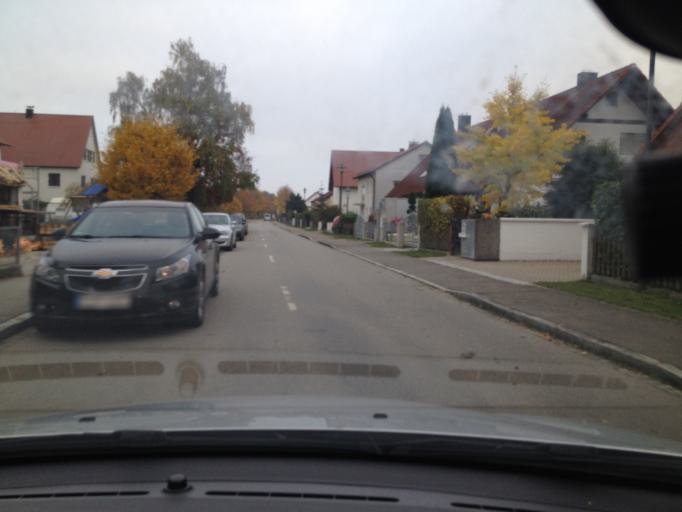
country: DE
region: Bavaria
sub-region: Swabia
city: Kleinaitingen
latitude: 48.2158
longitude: 10.8413
